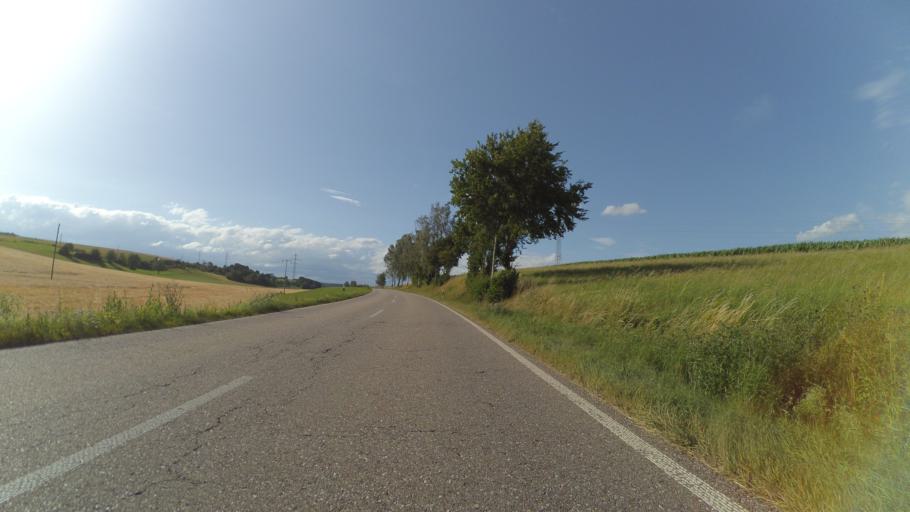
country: DE
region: Baden-Wuerttemberg
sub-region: Freiburg Region
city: Loffingen
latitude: 47.8696
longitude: 8.4056
